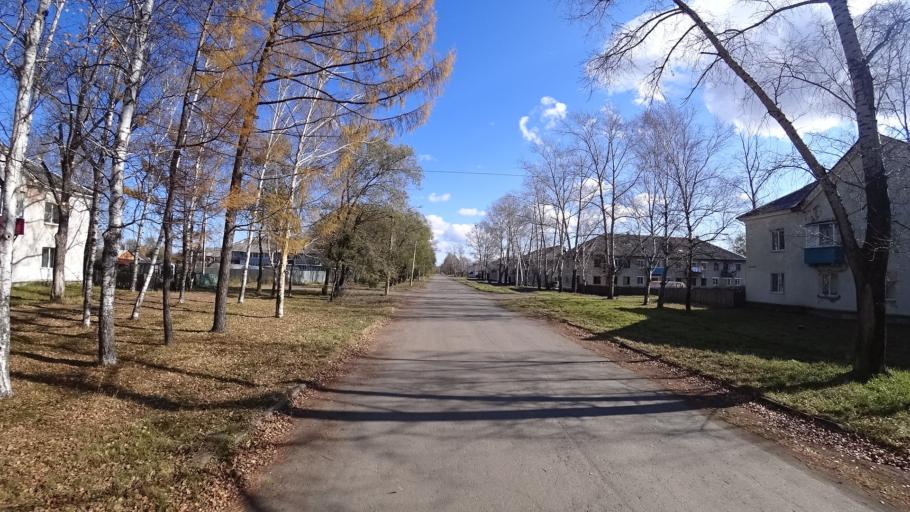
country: RU
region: Khabarovsk Krai
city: Amursk
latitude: 50.0991
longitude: 136.4945
